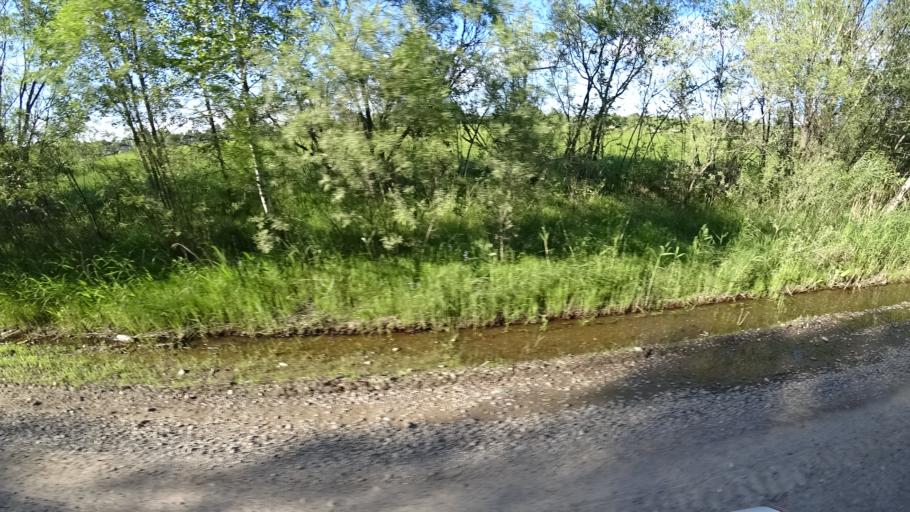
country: RU
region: Khabarovsk Krai
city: Khor
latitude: 47.8428
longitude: 134.9537
